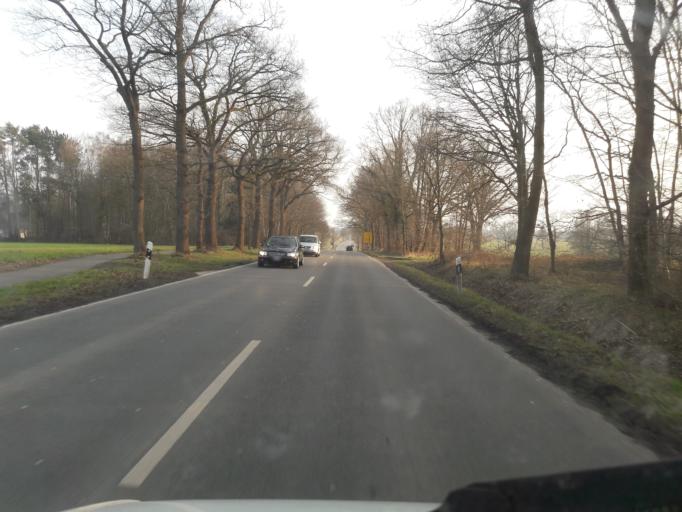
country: DE
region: North Rhine-Westphalia
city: Espelkamp
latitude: 52.3701
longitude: 8.6368
